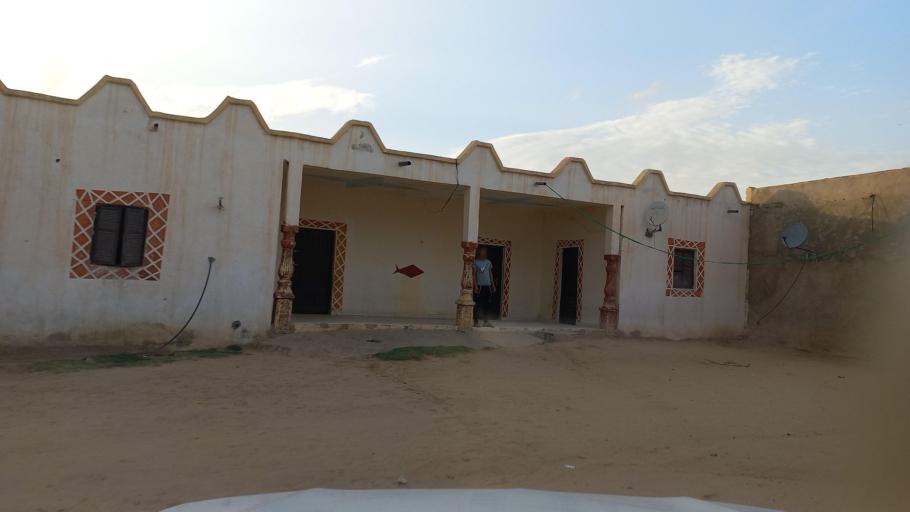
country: TN
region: Al Qasrayn
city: Kasserine
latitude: 35.2704
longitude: 9.0678
